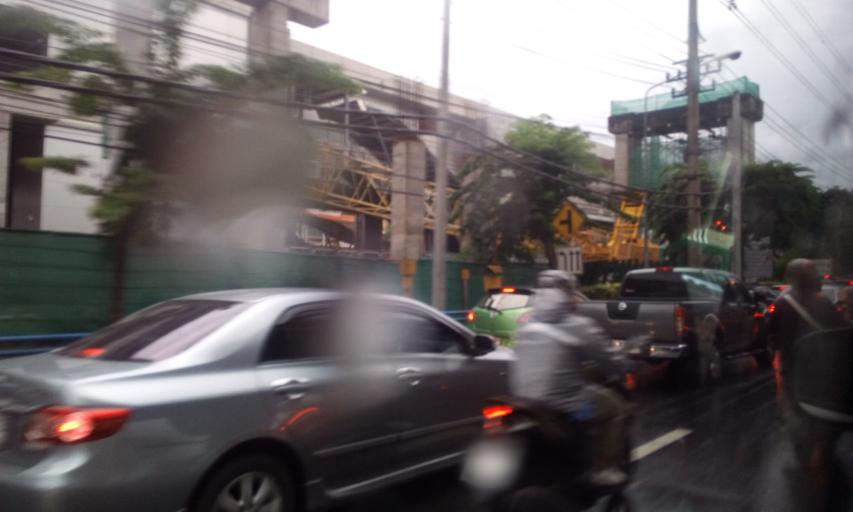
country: TH
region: Bangkok
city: Lak Si
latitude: 13.8869
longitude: 100.5825
